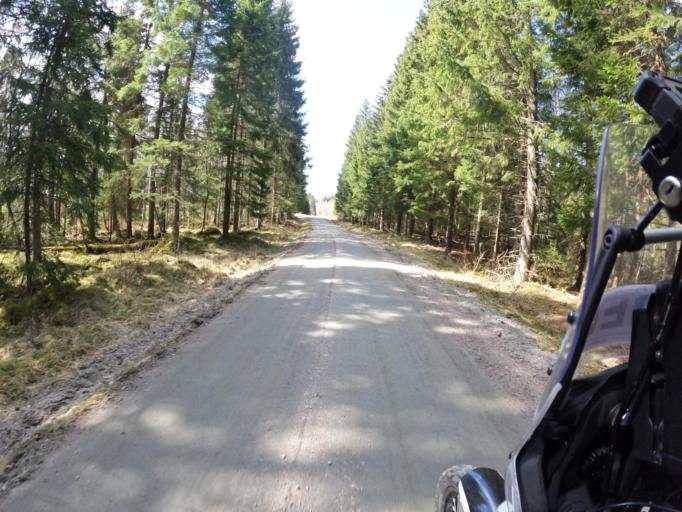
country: SE
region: Vaestra Goetaland
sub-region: Ulricehamns Kommun
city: Ulricehamn
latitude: 57.9287
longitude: 13.5612
